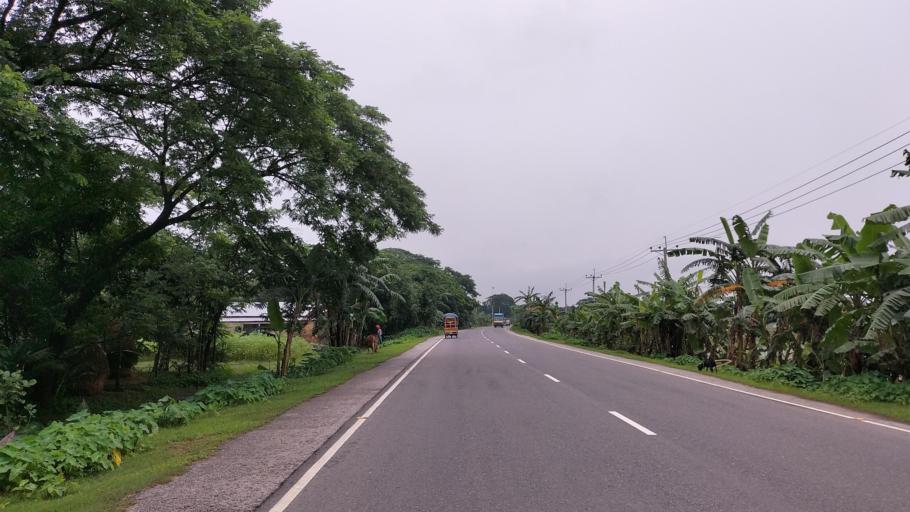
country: BD
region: Dhaka
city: Netrakona
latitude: 24.8523
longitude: 90.6185
